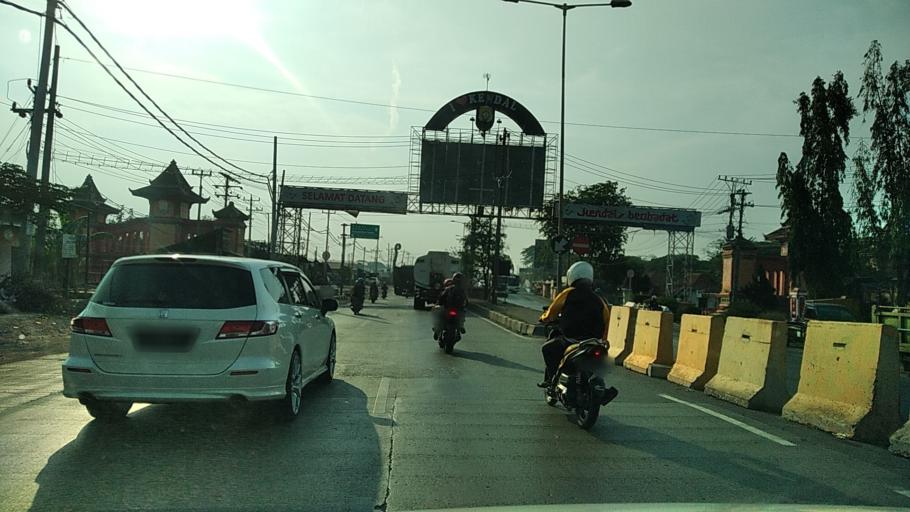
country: ID
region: Central Java
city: Semarang
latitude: -6.9683
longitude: 110.2850
